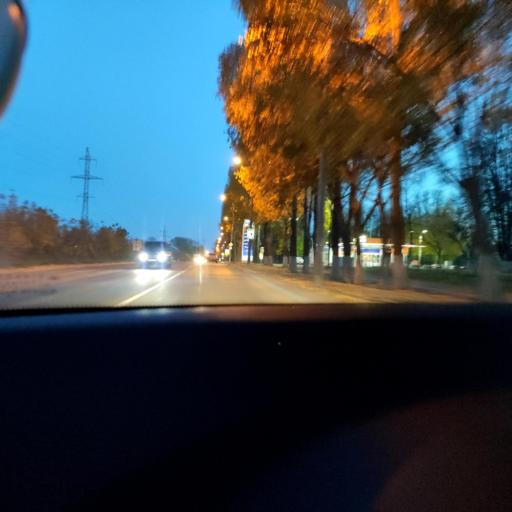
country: RU
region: Samara
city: Petra-Dubrava
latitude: 53.3070
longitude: 50.2787
